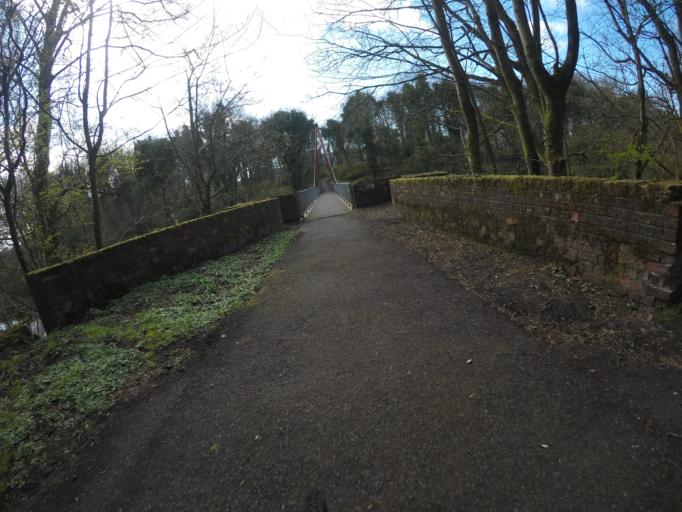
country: GB
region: Scotland
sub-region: North Ayrshire
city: Dreghorn
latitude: 55.5976
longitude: -4.6264
